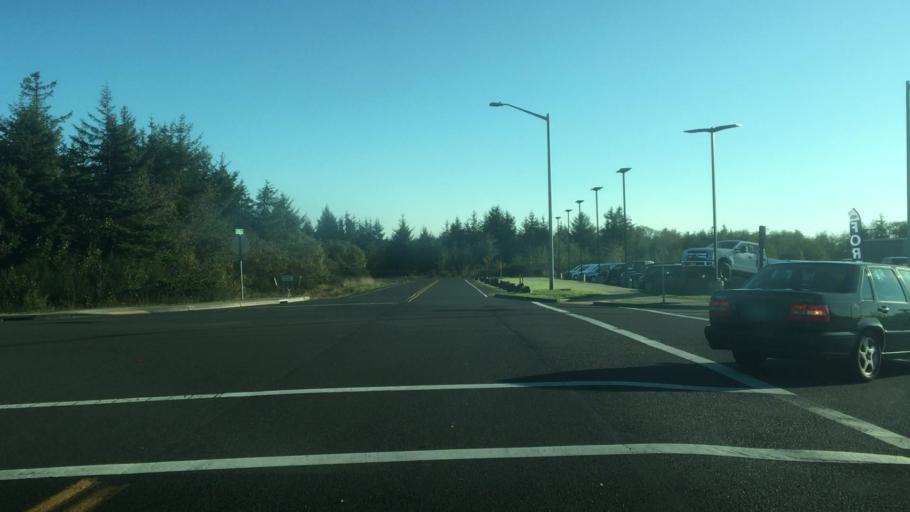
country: US
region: Oregon
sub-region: Clatsop County
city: Warrenton
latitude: 46.1453
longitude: -123.9123
